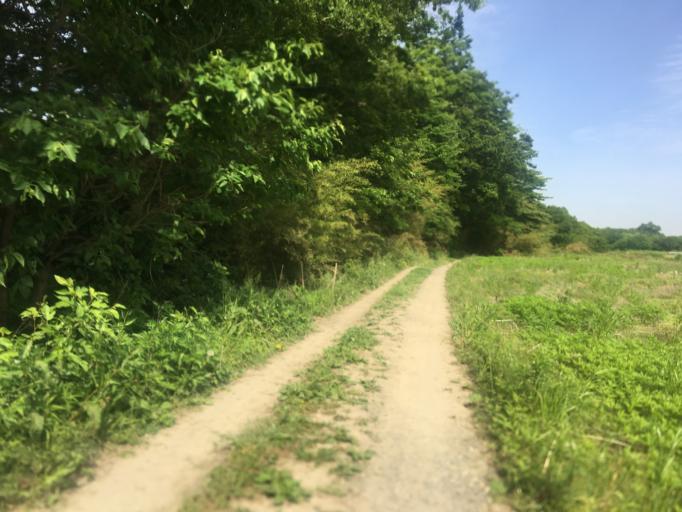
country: JP
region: Saitama
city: Shiki
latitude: 35.8502
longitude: 139.6043
